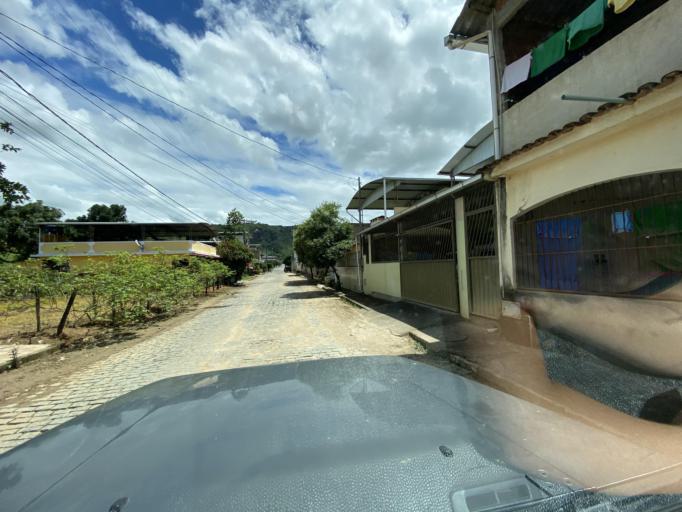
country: BR
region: Espirito Santo
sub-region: Jeronimo Monteiro
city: Jeronimo Monteiro
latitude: -20.7829
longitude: -41.3892
